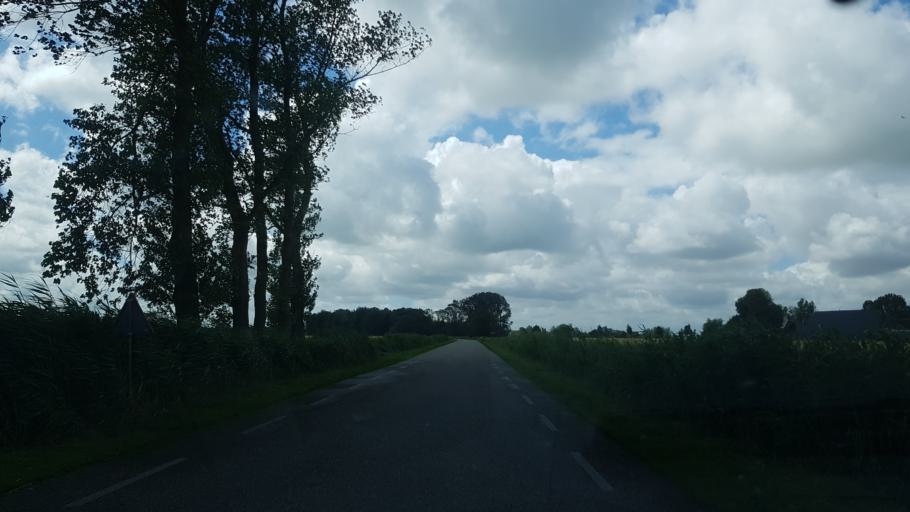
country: NL
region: Groningen
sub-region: Gemeente Winsum
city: Winsum
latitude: 53.3935
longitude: 6.5444
